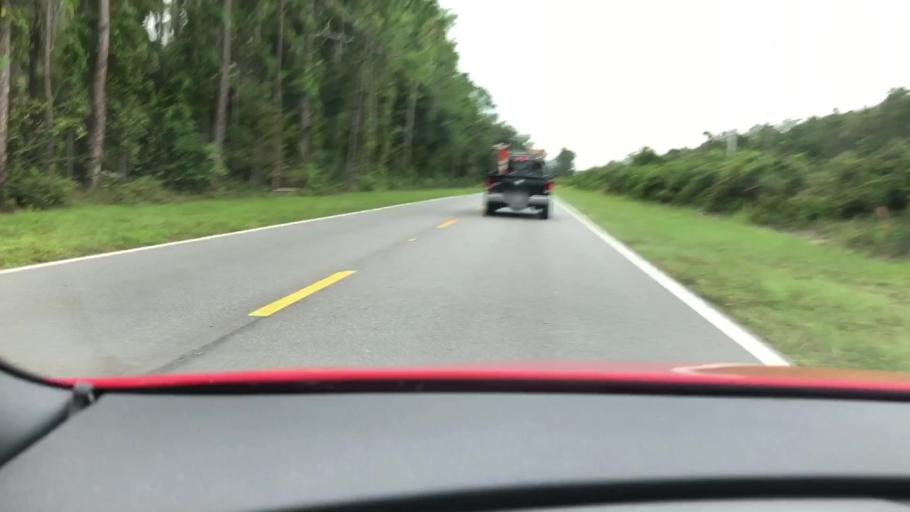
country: US
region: Florida
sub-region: Flagler County
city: Palm Coast
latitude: 29.5143
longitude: -81.1961
